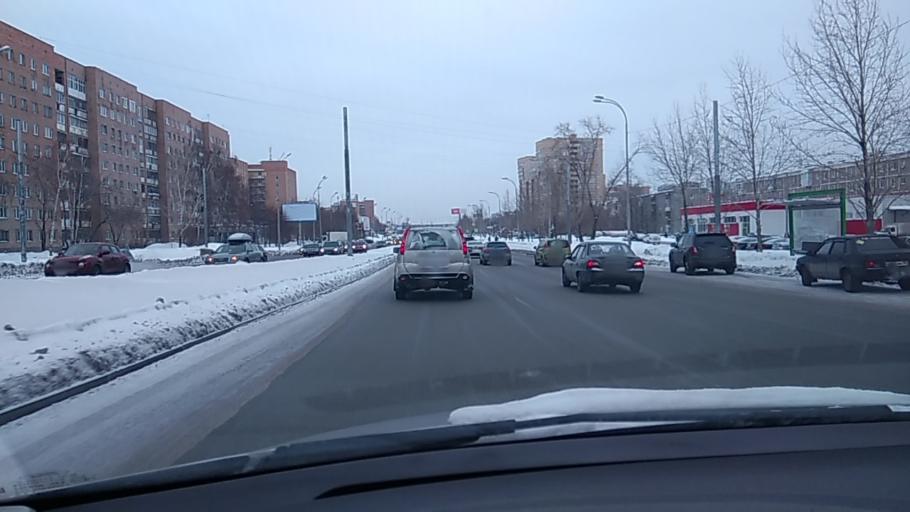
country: RU
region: Sverdlovsk
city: Yekaterinburg
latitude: 56.8350
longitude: 60.5619
